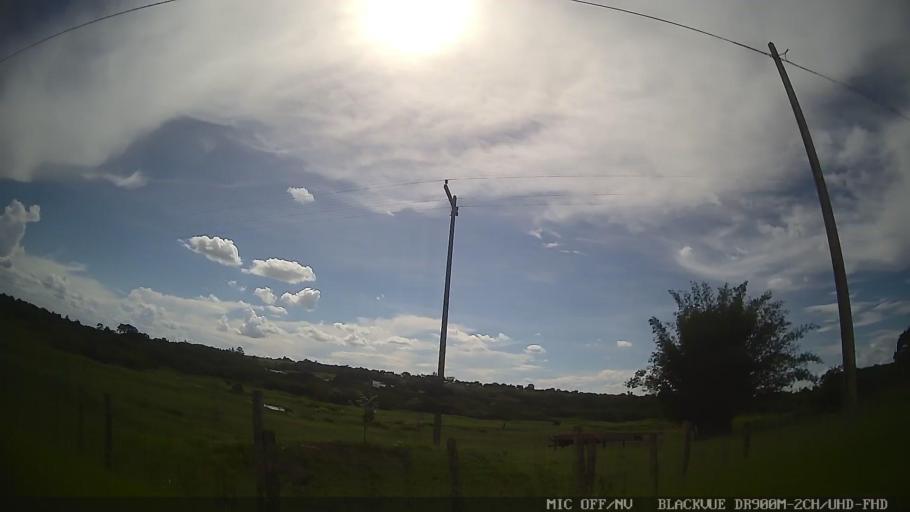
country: BR
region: Sao Paulo
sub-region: Conchas
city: Conchas
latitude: -23.0030
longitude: -48.0015
